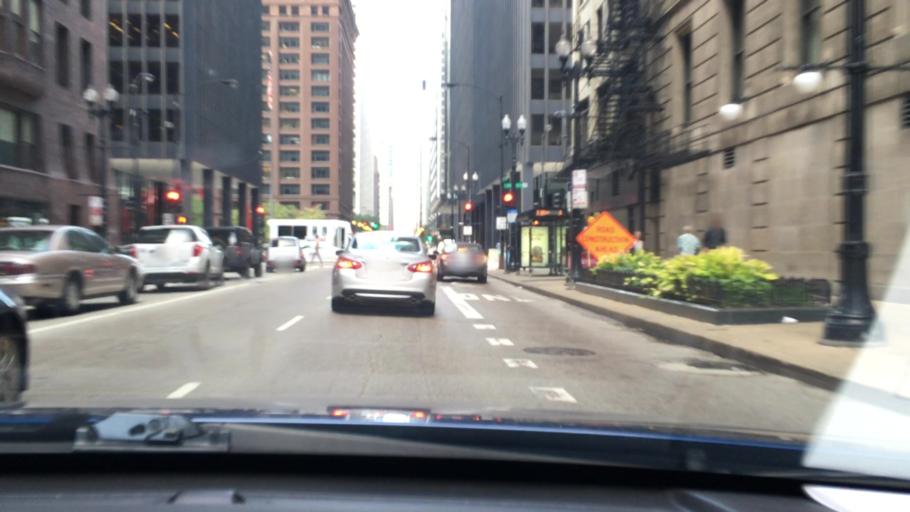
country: US
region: Illinois
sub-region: Cook County
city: Chicago
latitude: 41.8776
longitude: -87.6293
